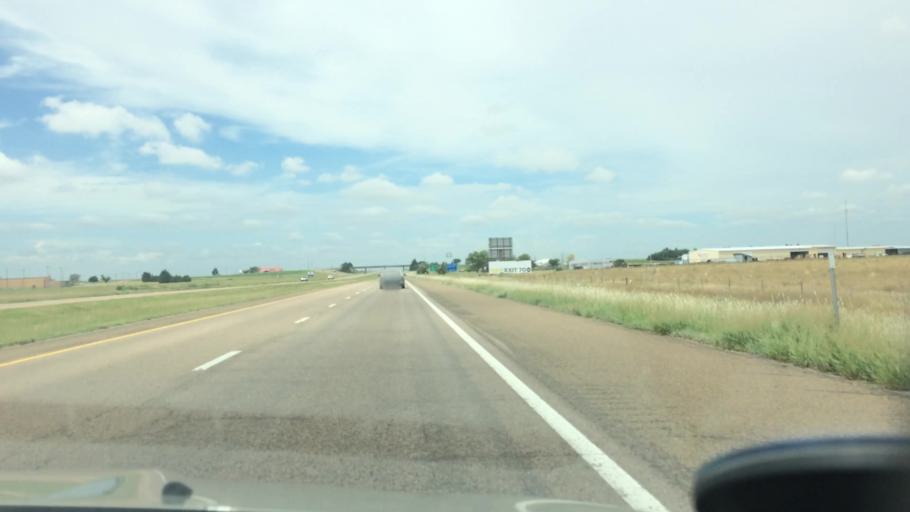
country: US
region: Kansas
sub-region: Gove County
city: Gove
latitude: 39.1077
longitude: -100.4686
